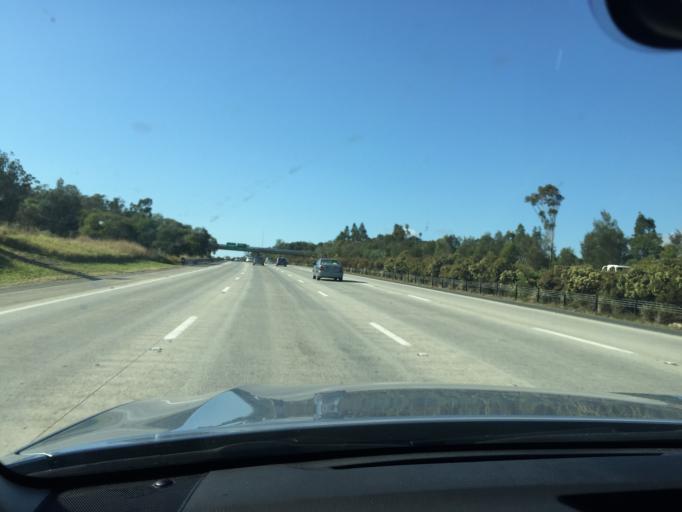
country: AU
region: Queensland
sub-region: Gold Coast
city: Ormeau Hills
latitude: -27.8033
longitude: 153.2638
